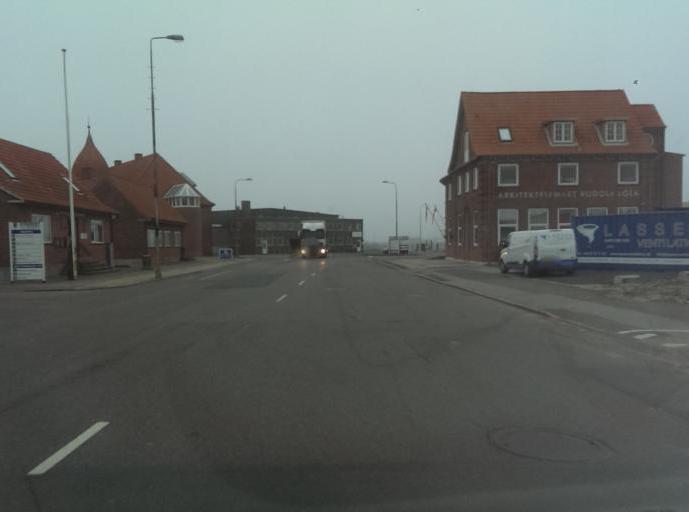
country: DK
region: South Denmark
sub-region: Esbjerg Kommune
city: Esbjerg
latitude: 55.4723
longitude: 8.4294
